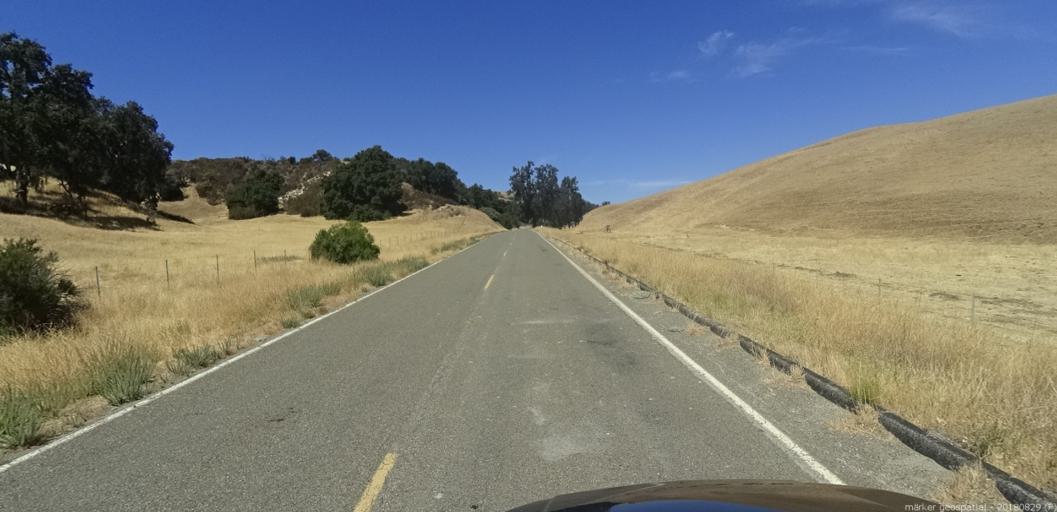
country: US
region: California
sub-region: San Luis Obispo County
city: Lake Nacimiento
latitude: 35.8387
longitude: -121.0397
